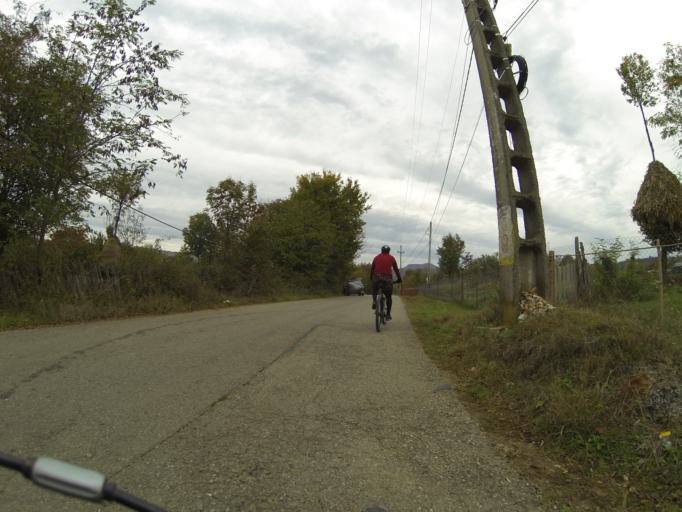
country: RO
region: Gorj
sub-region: Comuna Tismana
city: Sohodol
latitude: 45.0448
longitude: 22.8964
